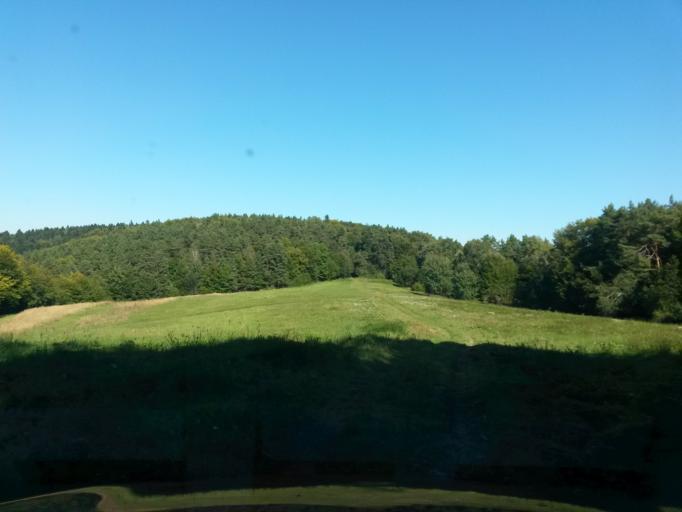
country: SK
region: Presovsky
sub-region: Okres Presov
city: Presov
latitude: 48.9784
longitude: 21.1478
